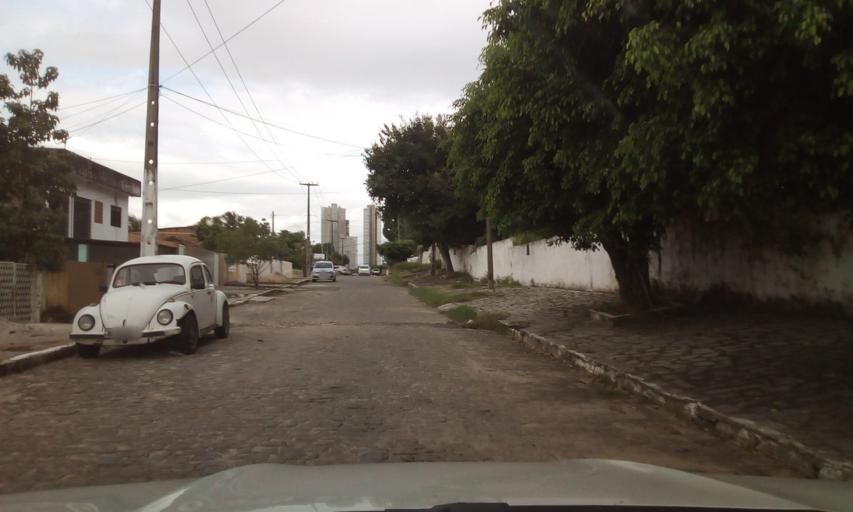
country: BR
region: Paraiba
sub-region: Joao Pessoa
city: Joao Pessoa
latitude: -7.1287
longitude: -34.8405
